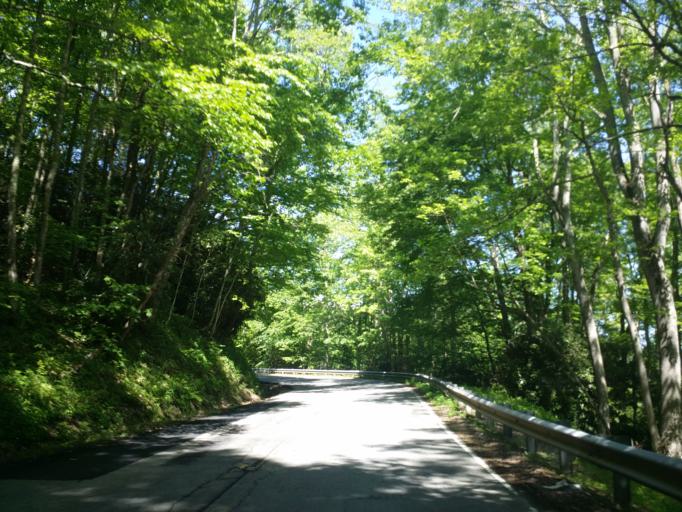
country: US
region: North Carolina
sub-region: Madison County
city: Marshall
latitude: 35.7204
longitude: -82.8386
